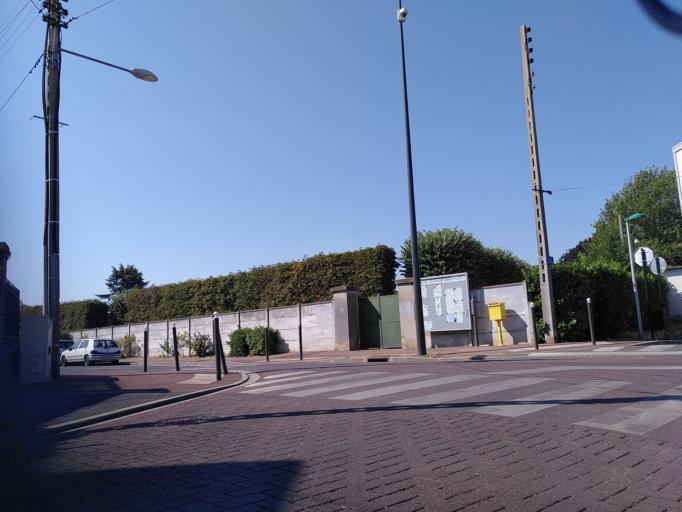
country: FR
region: Ile-de-France
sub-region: Departement de l'Essonne
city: Paray-Vieille-Poste
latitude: 48.6964
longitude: 2.3594
